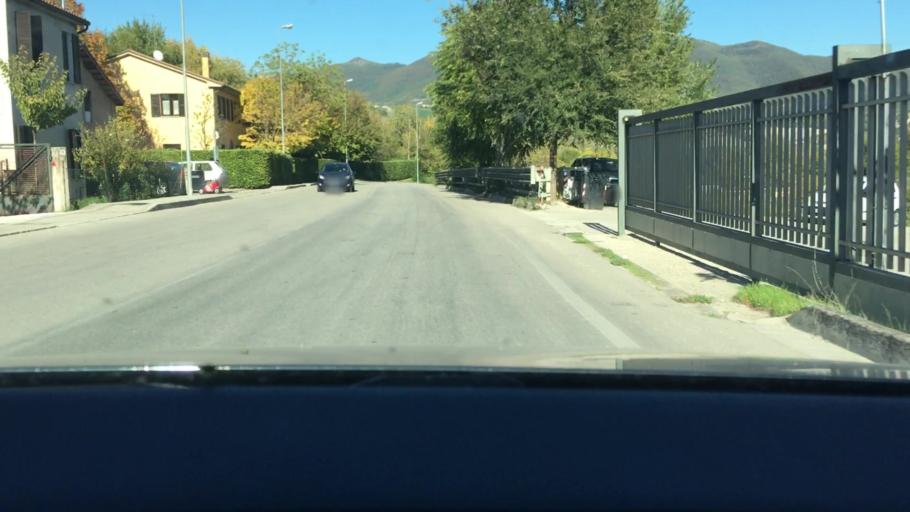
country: IT
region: The Marches
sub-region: Provincia di Ancona
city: Fabriano
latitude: 43.3506
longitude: 12.9163
